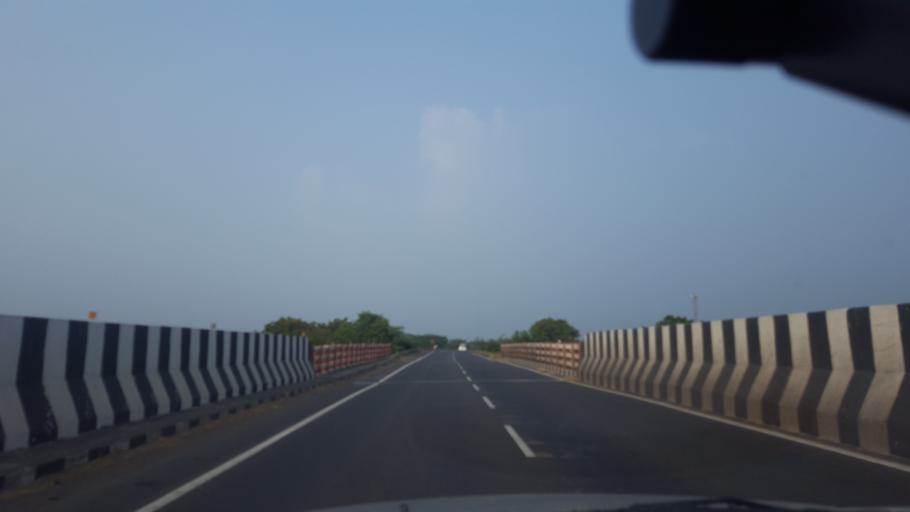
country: IN
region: Andhra Pradesh
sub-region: West Godavari
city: Tadepallegudem
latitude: 16.8274
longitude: 81.4664
